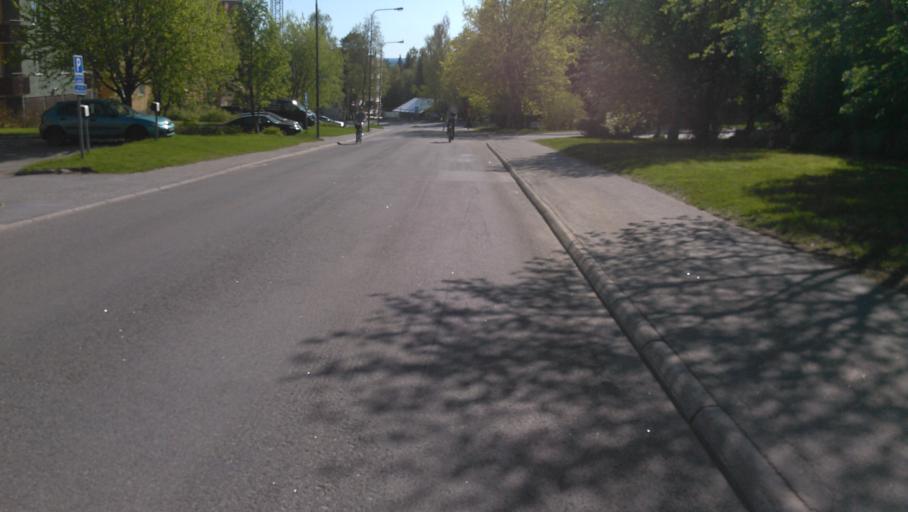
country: SE
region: Vaesterbotten
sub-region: Umea Kommun
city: Umea
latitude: 63.8273
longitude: 20.2965
